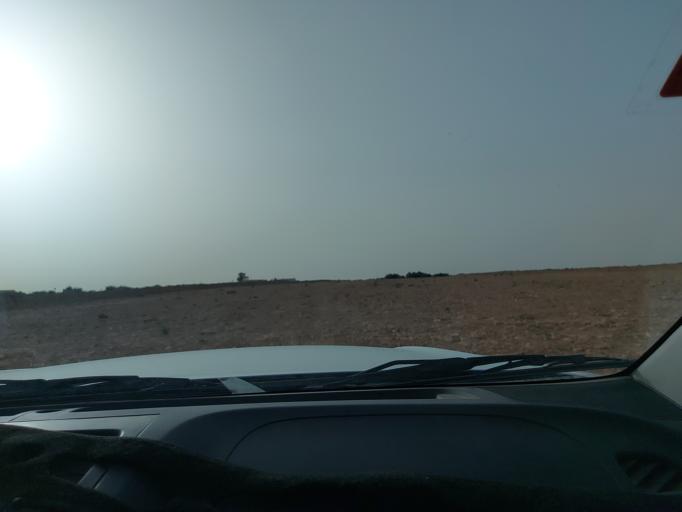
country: TN
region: Madanin
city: Medenine
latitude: 33.3381
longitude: 10.5944
